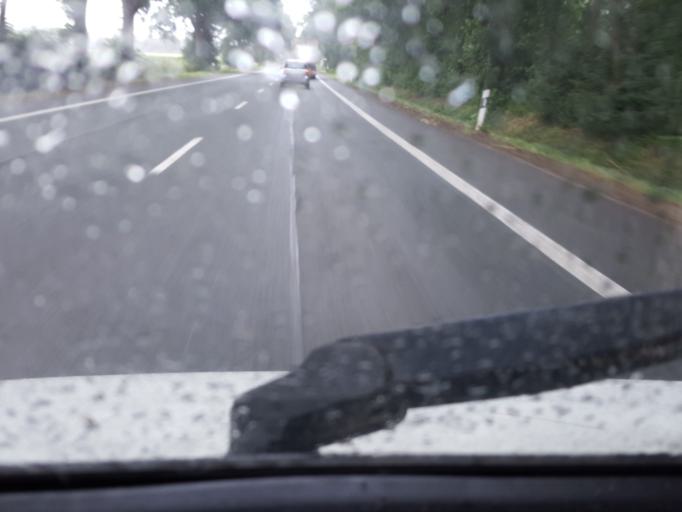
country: DE
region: North Rhine-Westphalia
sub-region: Regierungsbezirk Detmold
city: Petershagen
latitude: 52.3372
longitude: 8.9338
